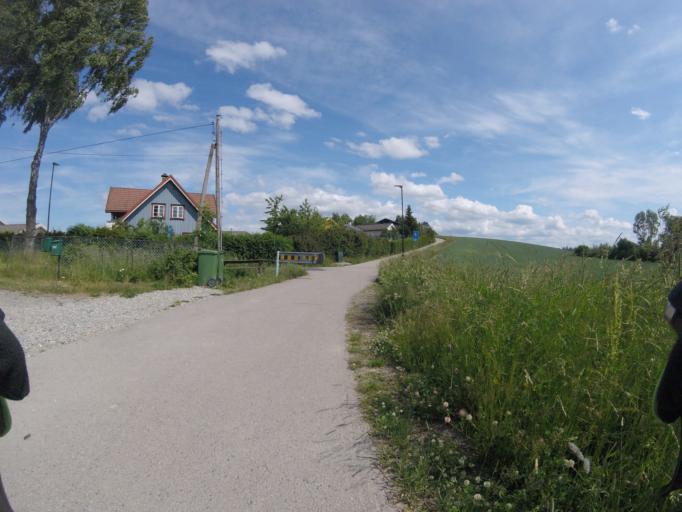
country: NO
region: Akershus
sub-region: Skedsmo
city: Lillestrom
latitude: 59.9822
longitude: 11.0317
